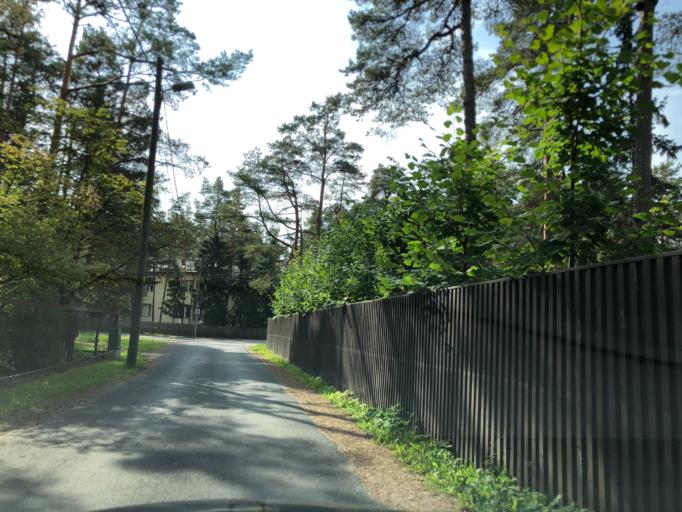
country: EE
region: Harju
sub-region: Tallinna linn
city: Tallinn
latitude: 59.3805
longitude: 24.6940
